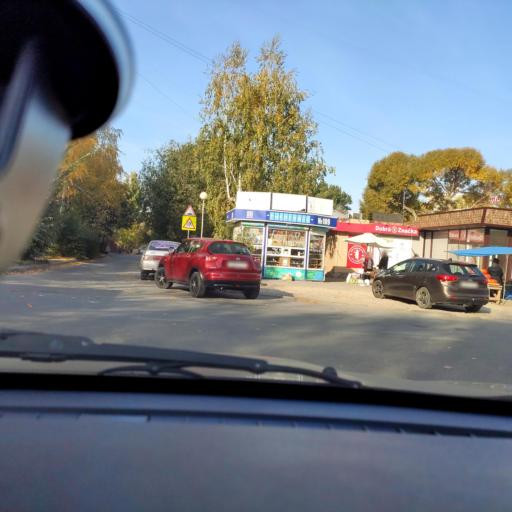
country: RU
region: Samara
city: Tol'yatti
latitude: 53.5102
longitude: 49.2617
